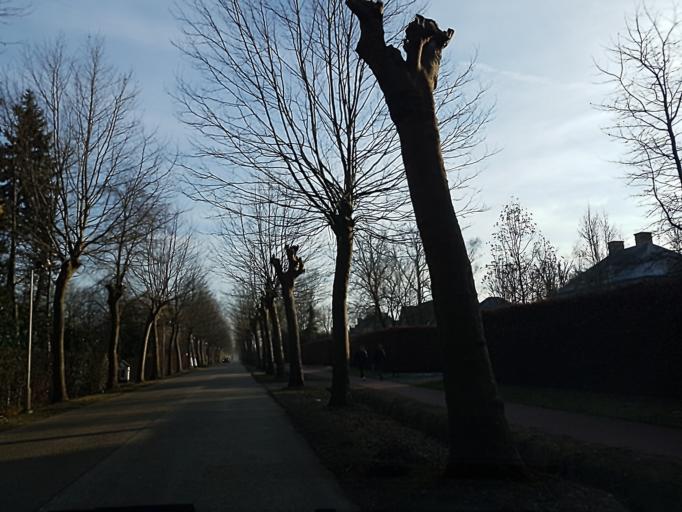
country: BE
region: Flanders
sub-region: Provincie Antwerpen
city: Schilde
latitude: 51.2570
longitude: 4.5972
